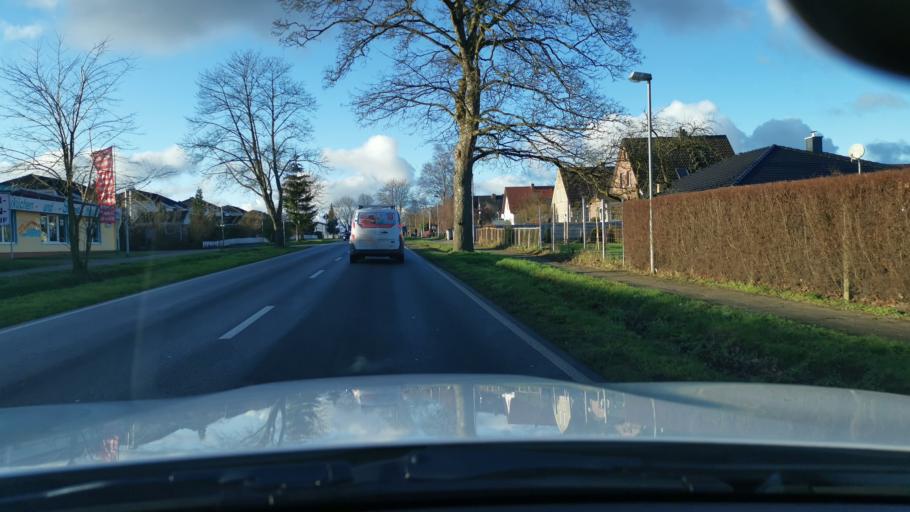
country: DE
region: Mecklenburg-Vorpommern
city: Tessin
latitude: 54.0301
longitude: 12.4549
